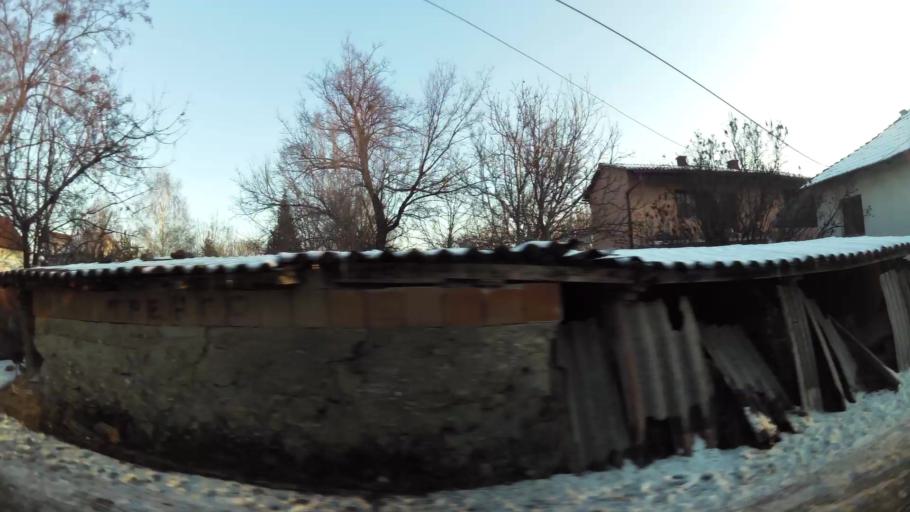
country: MK
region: Kisela Voda
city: Kisela Voda
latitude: 41.9779
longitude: 21.4950
